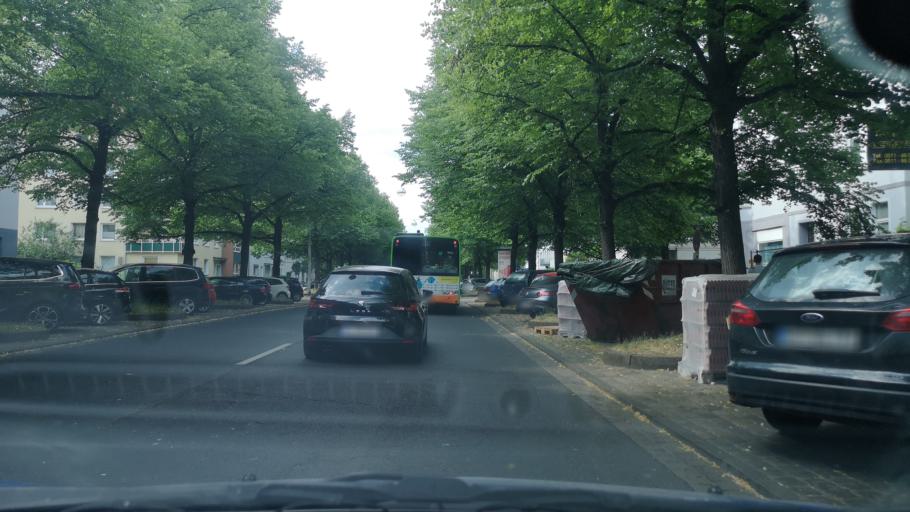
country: DE
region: Lower Saxony
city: Hannover
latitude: 52.3939
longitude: 9.7456
